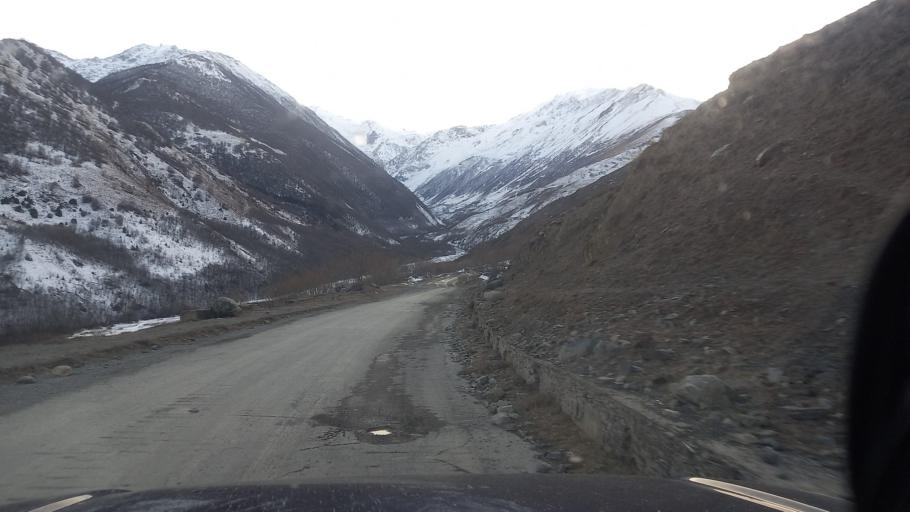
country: RU
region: Ingushetiya
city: Dzhayrakh
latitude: 42.8408
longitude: 44.5124
